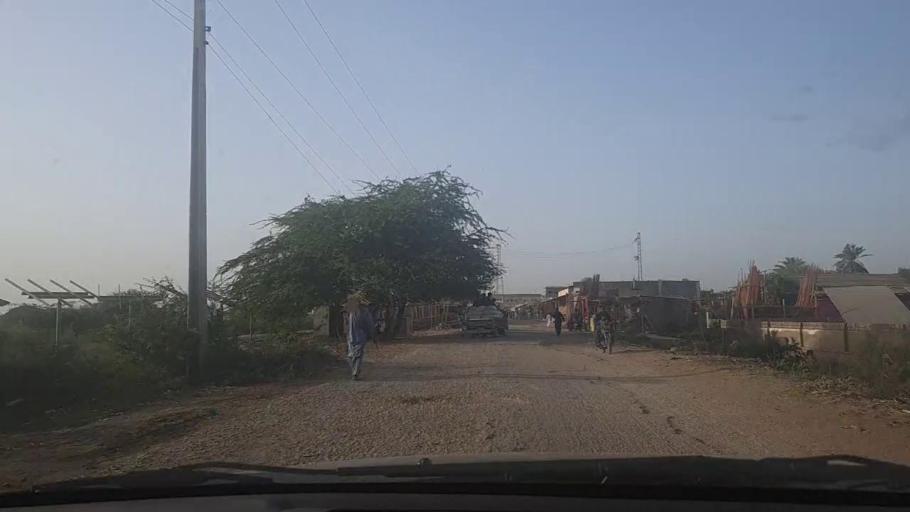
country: PK
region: Sindh
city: Keti Bandar
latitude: 24.2973
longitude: 67.6077
